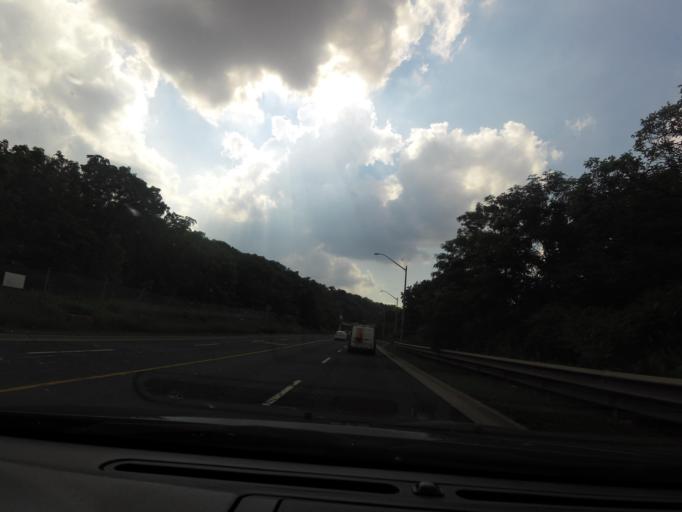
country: CA
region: Ontario
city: Hamilton
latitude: 43.2338
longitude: -79.8226
